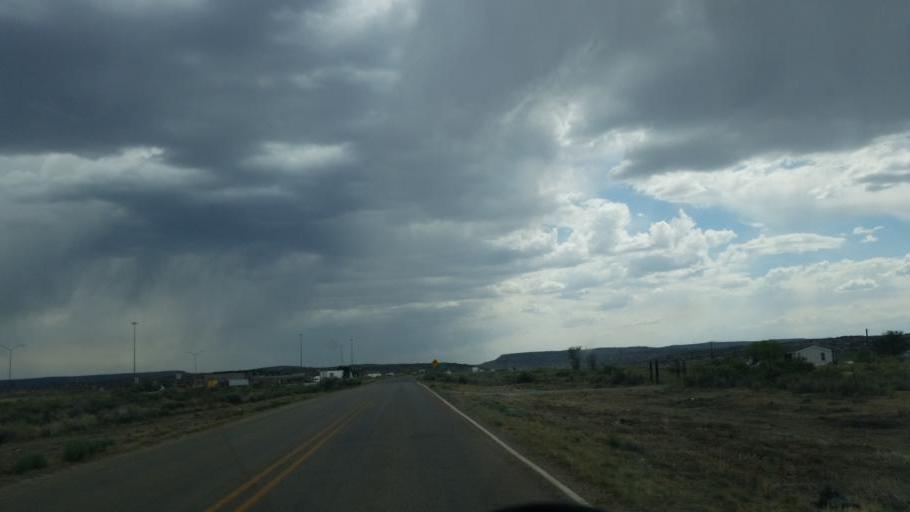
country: US
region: New Mexico
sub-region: McKinley County
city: Gallup
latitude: 35.4885
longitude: -108.8986
